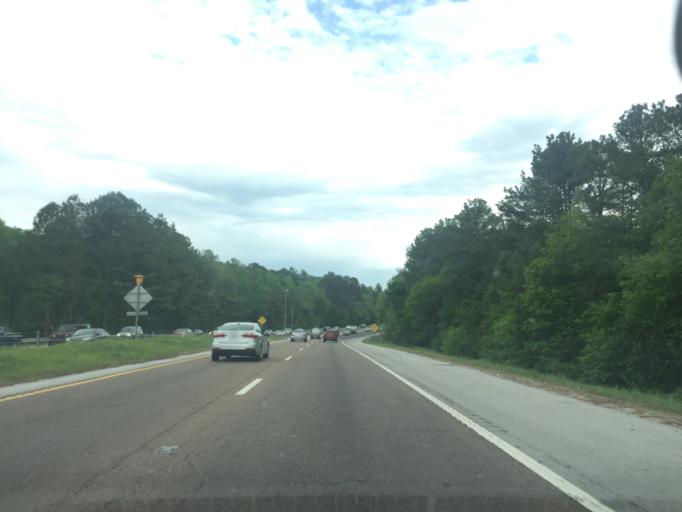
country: US
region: Tennessee
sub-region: Hamilton County
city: East Chattanooga
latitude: 35.1161
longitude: -85.2325
